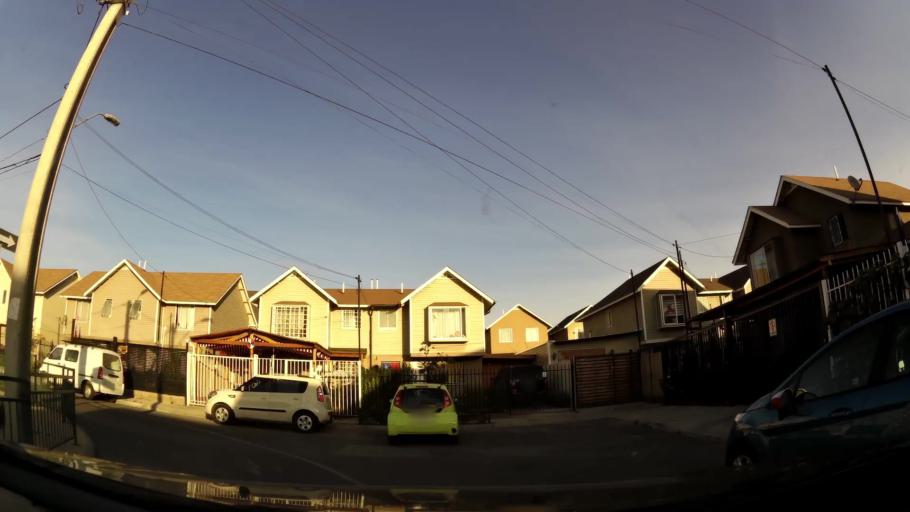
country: CL
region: Santiago Metropolitan
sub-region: Provincia de Cordillera
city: Puente Alto
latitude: -33.5995
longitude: -70.5474
